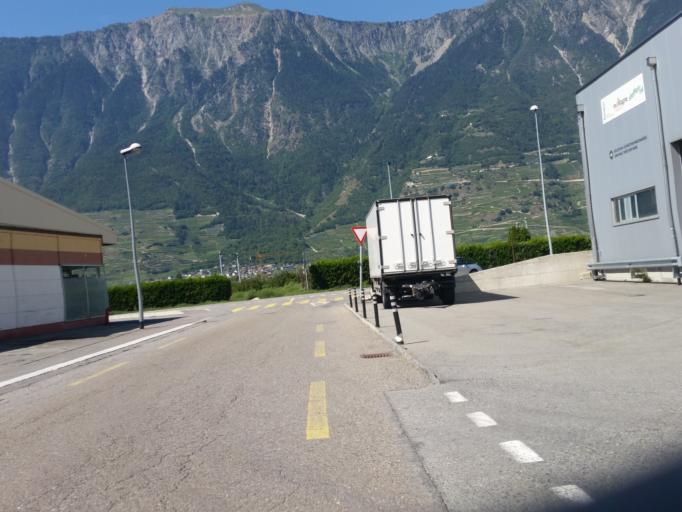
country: CH
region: Valais
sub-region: Martigny District
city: Charrat-les-Chenes
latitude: 46.1288
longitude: 7.1336
